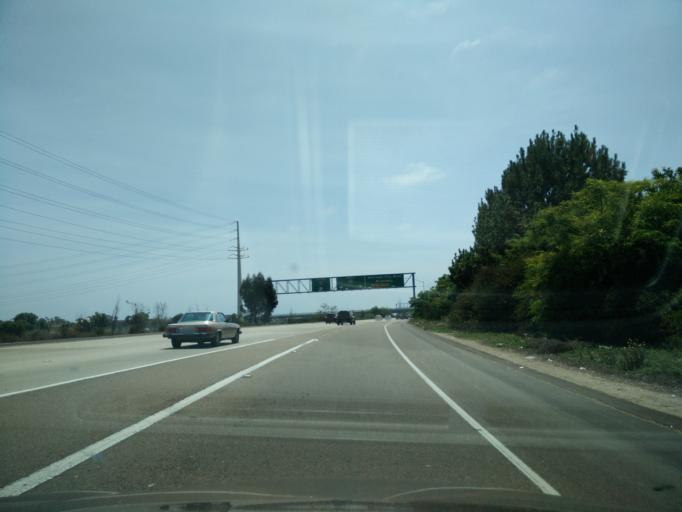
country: US
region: California
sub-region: San Diego County
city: Chula Vista
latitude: 32.6554
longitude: -117.0920
